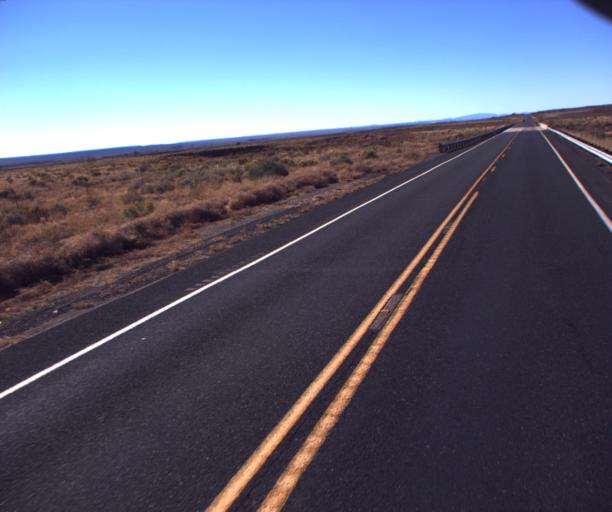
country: US
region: Arizona
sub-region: Coconino County
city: Fredonia
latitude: 36.9292
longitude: -112.5626
